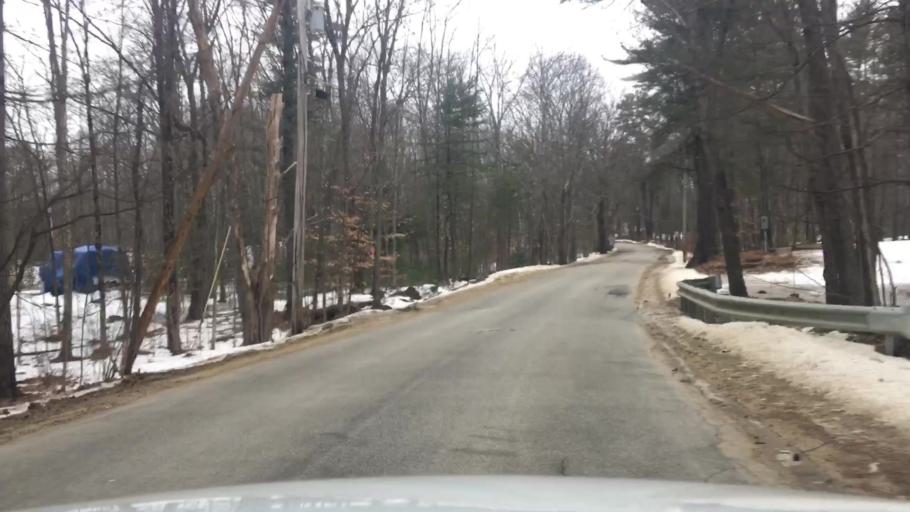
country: US
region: New Hampshire
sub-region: Strafford County
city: Rochester
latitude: 43.3489
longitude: -70.9631
